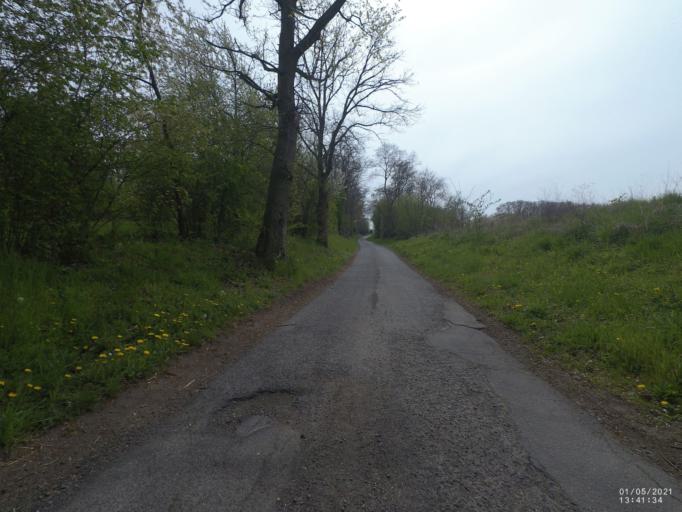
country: DE
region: Rheinland-Pfalz
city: Kettig
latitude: 50.3846
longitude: 7.4596
